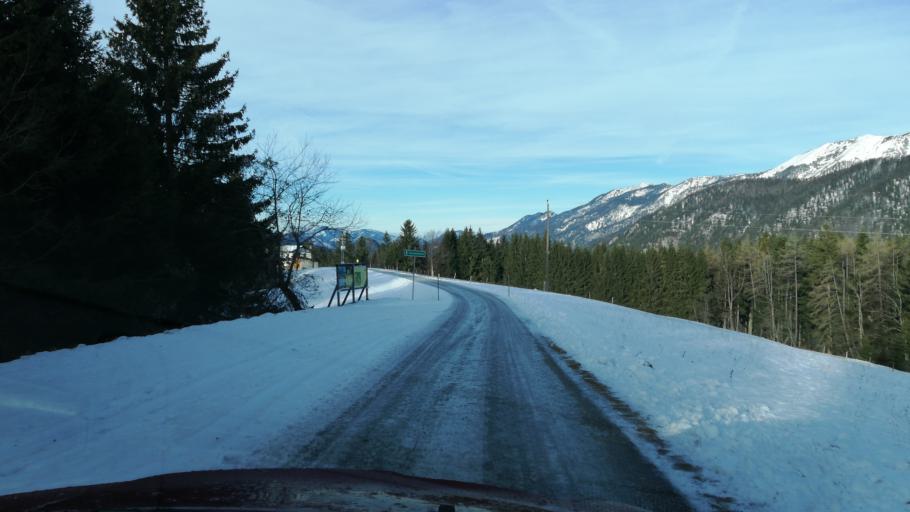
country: AT
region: Upper Austria
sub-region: Politischer Bezirk Kirchdorf an der Krems
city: Rossleithen
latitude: 47.7267
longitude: 14.3473
